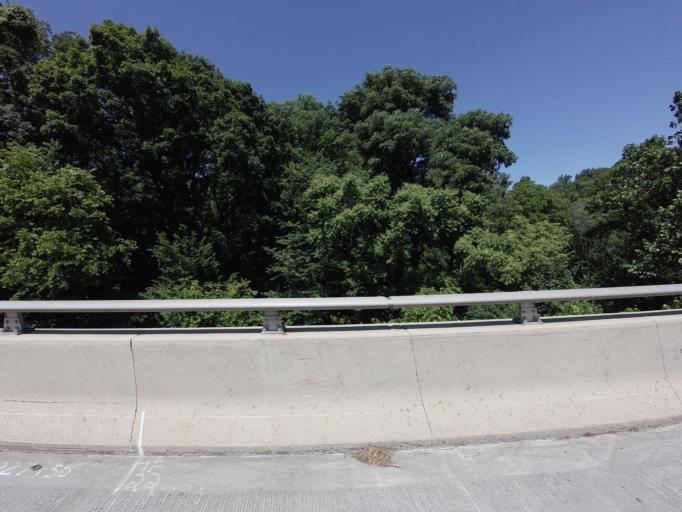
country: US
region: Maryland
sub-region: Frederick County
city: Brunswick
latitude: 39.3342
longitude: -77.6876
